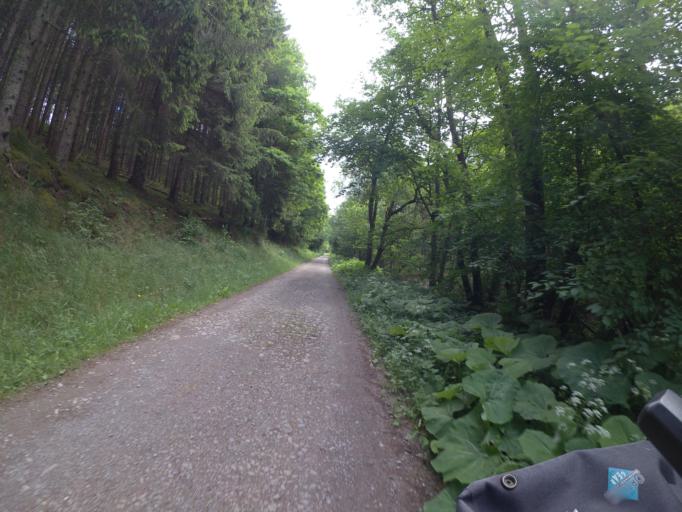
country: DE
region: North Rhine-Westphalia
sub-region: Regierungsbezirk Koln
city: Hellenthal
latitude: 50.4506
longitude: 6.4154
